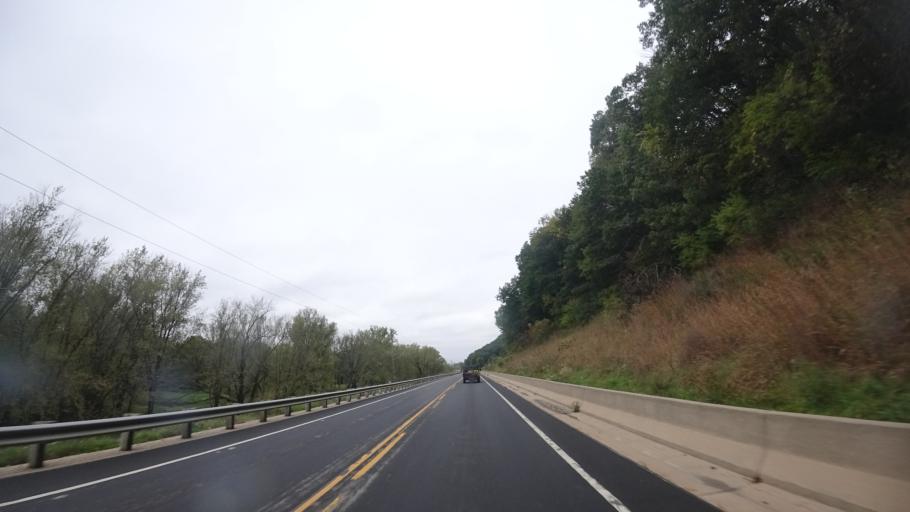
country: US
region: Wisconsin
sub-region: Grant County
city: Boscobel
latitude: 43.1344
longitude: -90.7470
